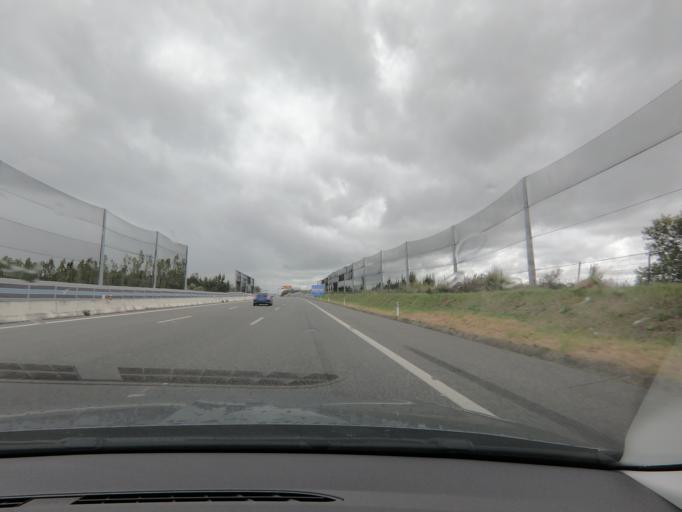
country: PT
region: Lisbon
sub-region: Sintra
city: Sintra
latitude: 38.7660
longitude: -9.3729
